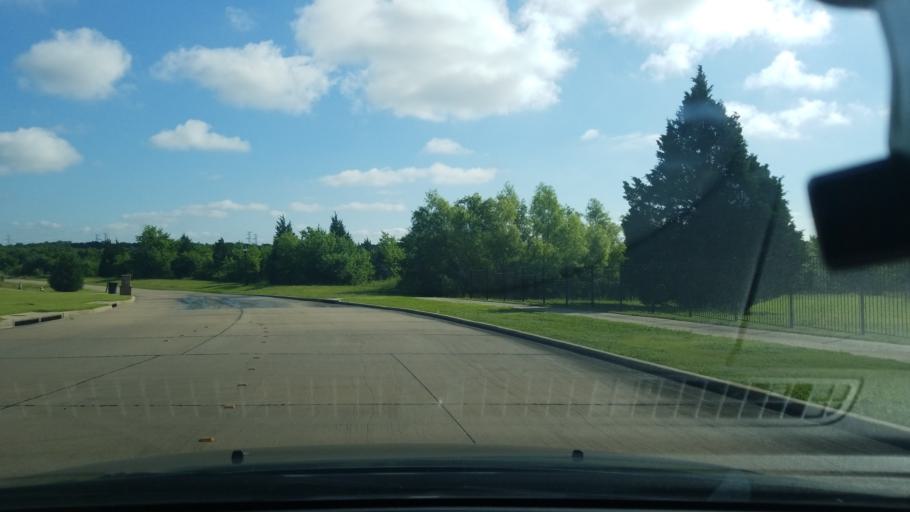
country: US
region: Texas
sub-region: Dallas County
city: Sunnyvale
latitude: 32.8080
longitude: -96.5559
